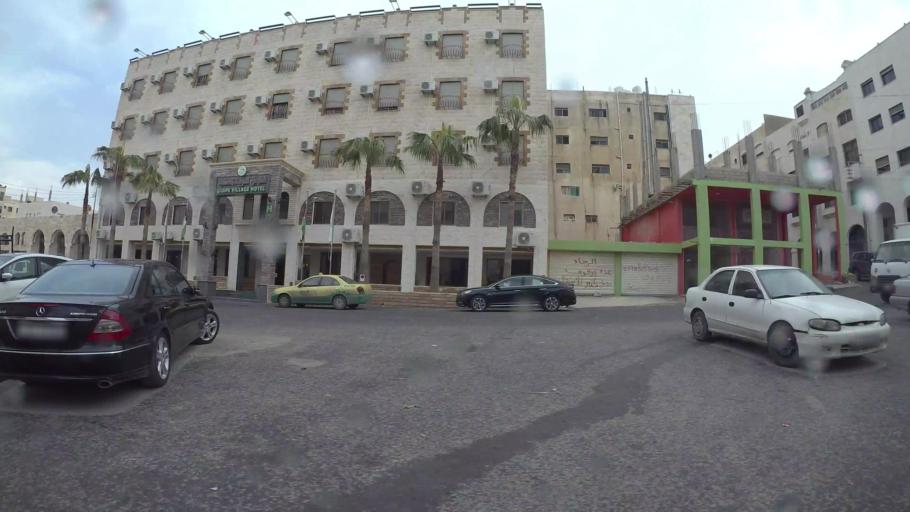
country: JO
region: Amman
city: Umm as Summaq
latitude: 31.8892
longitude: 35.8577
